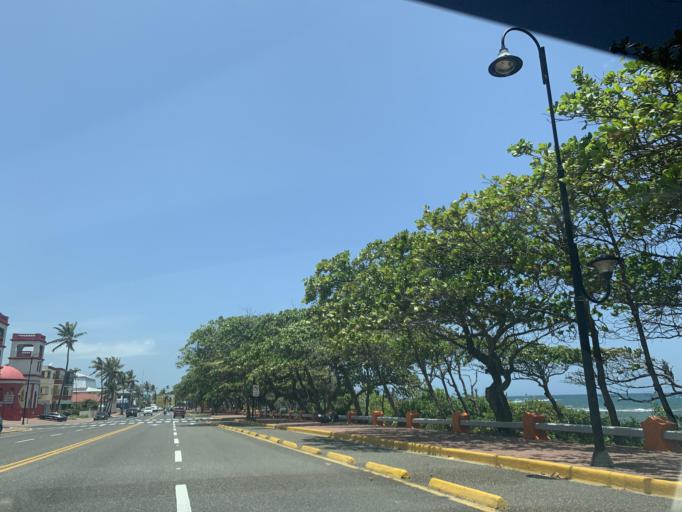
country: DO
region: Puerto Plata
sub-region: Puerto Plata
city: Puerto Plata
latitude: 19.7989
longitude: -70.6894
